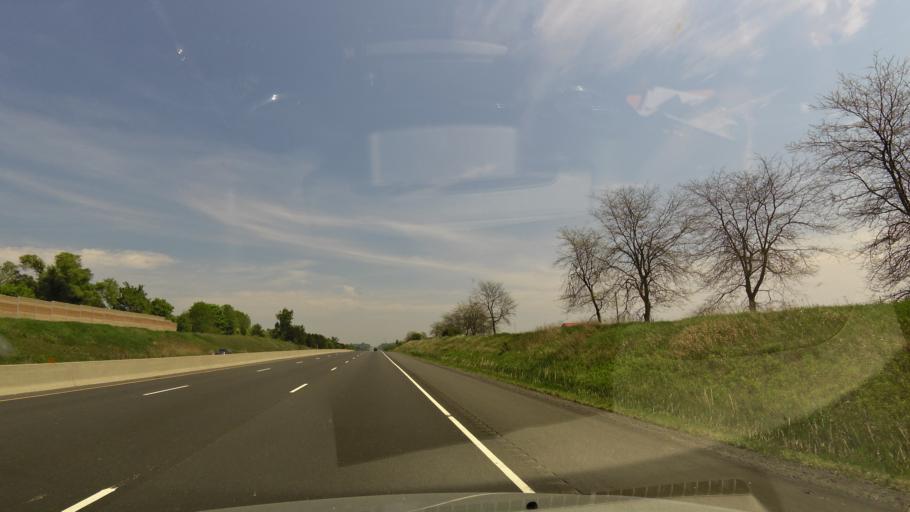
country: CA
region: Ontario
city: Oshawa
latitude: 43.9082
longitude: -78.5968
